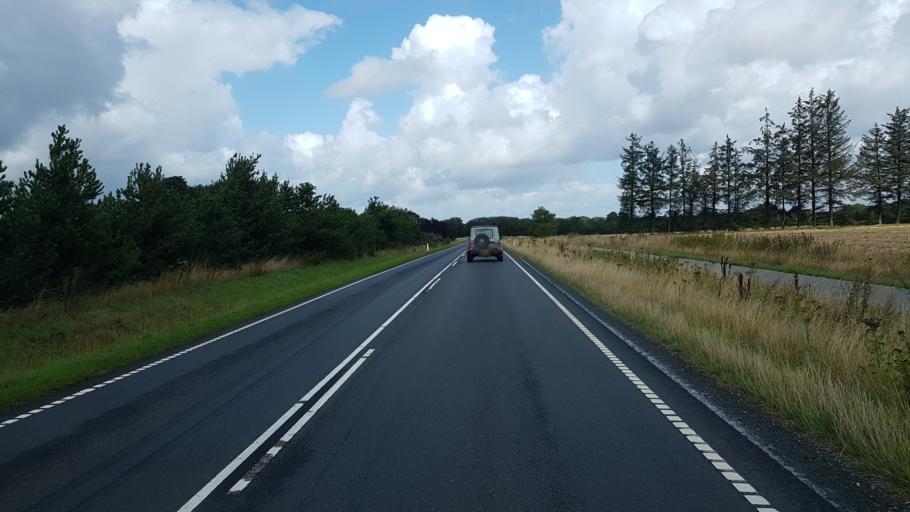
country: DK
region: South Denmark
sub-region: Vejen Kommune
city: Vejen
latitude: 55.5044
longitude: 9.1330
